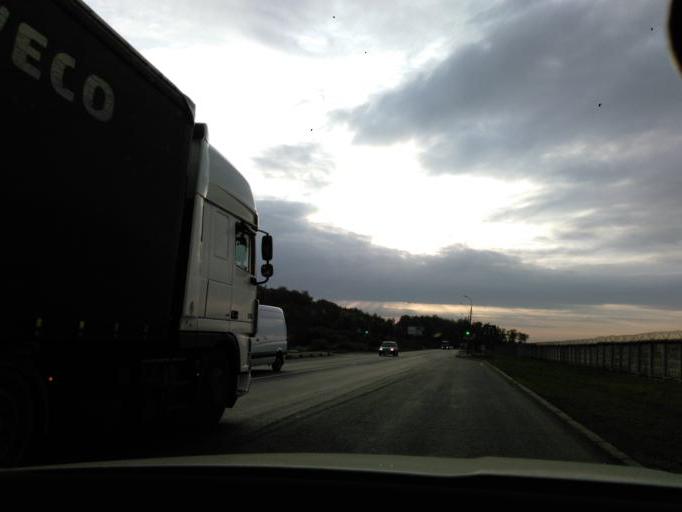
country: RU
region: Moskovskaya
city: Lobnya
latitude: 55.9829
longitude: 37.4449
